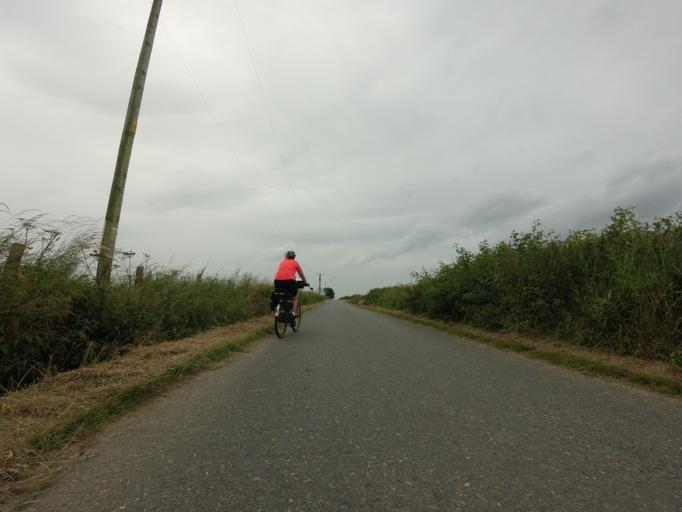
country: GB
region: Scotland
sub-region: Aberdeenshire
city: Portsoy
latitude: 57.6627
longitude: -2.7519
